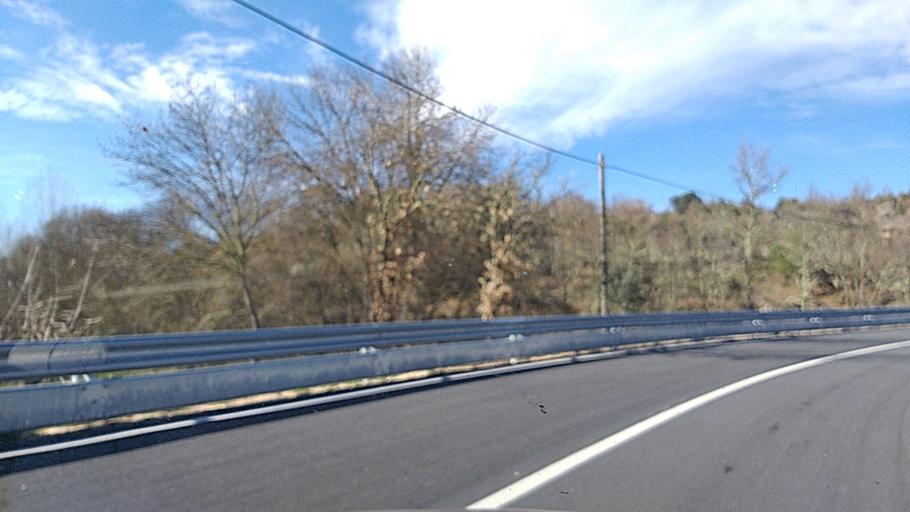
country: ES
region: Castille and Leon
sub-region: Provincia de Salamanca
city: Fuentes de Onoro
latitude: 40.6006
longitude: -6.9330
